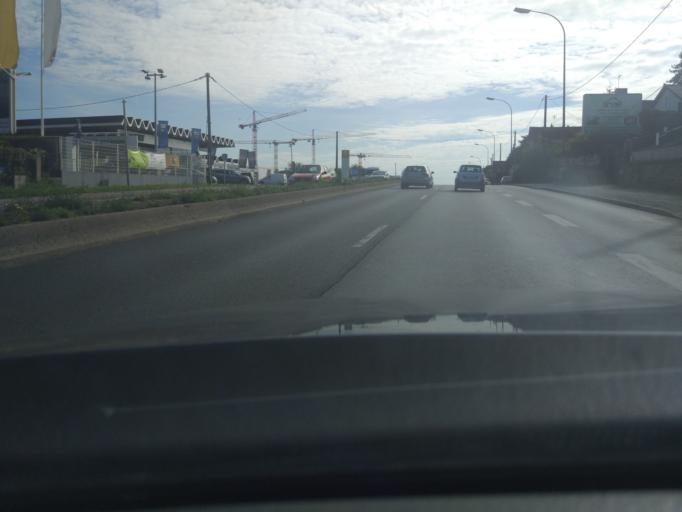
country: FR
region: Ile-de-France
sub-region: Departement de l'Essonne
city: La Ville-du-Bois
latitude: 48.6485
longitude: 2.2714
